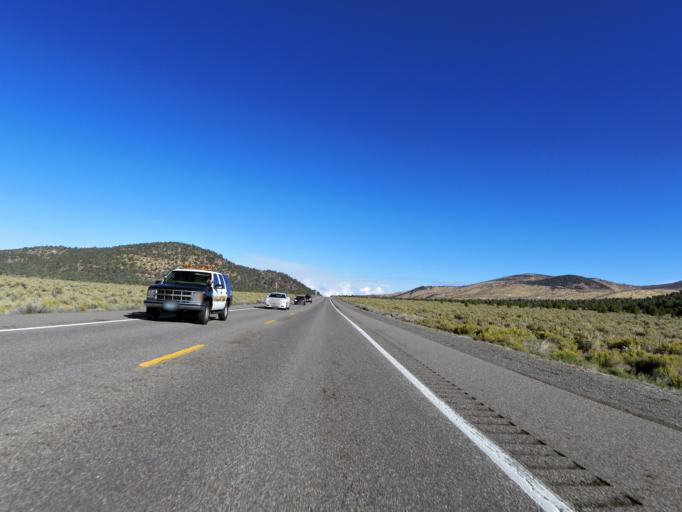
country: US
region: Nevada
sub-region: Douglas County
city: Gardnerville Ranchos
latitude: 38.7963
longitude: -119.6018
